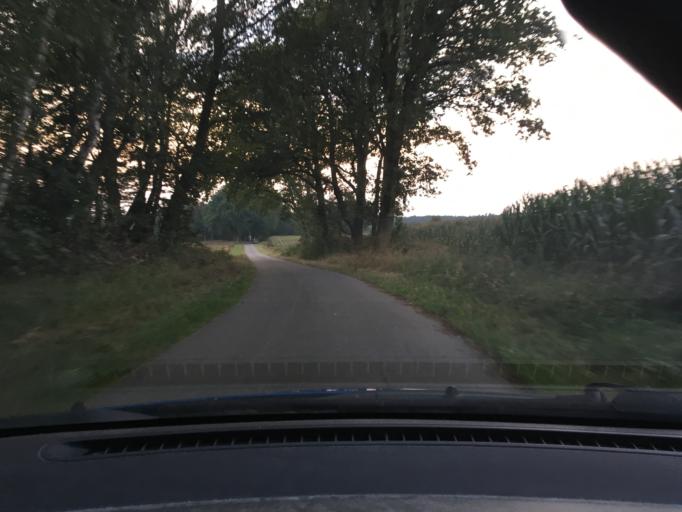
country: DE
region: Lower Saxony
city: Altenmedingen
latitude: 53.1808
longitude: 10.6249
